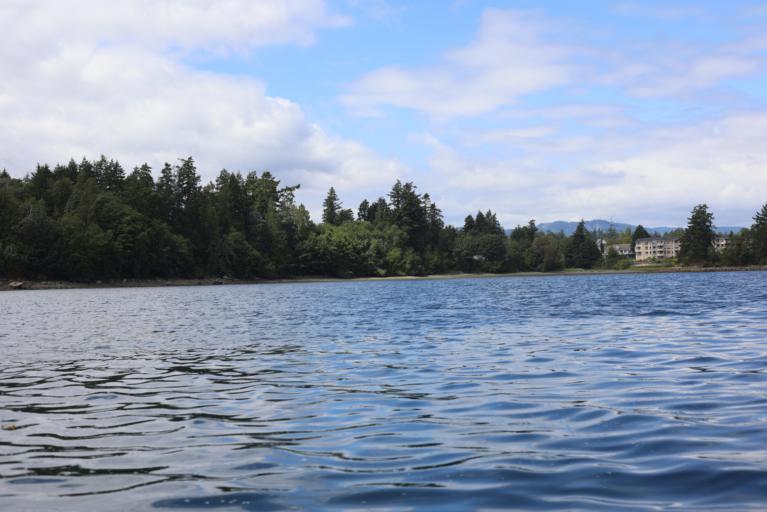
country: CA
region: British Columbia
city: North Saanich
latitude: 48.5945
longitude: -123.3837
